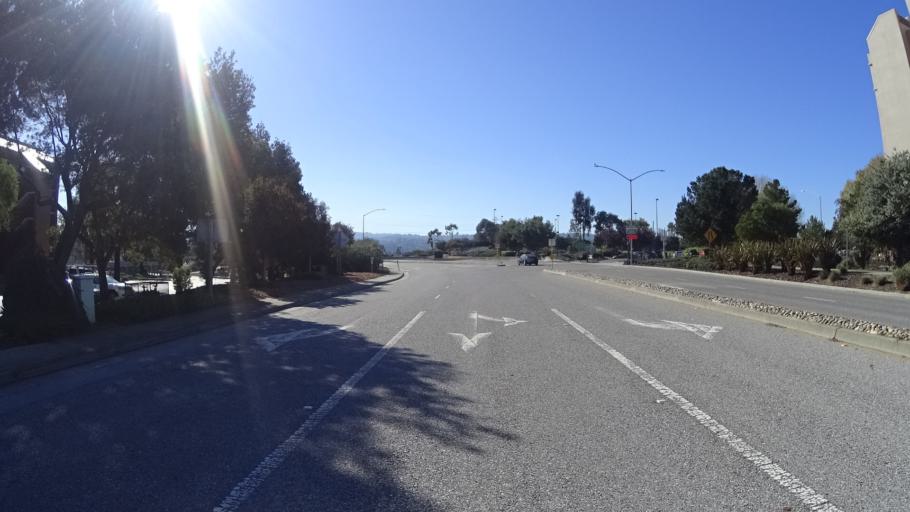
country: US
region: California
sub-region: San Mateo County
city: Burlingame
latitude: 37.5899
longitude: -122.3506
